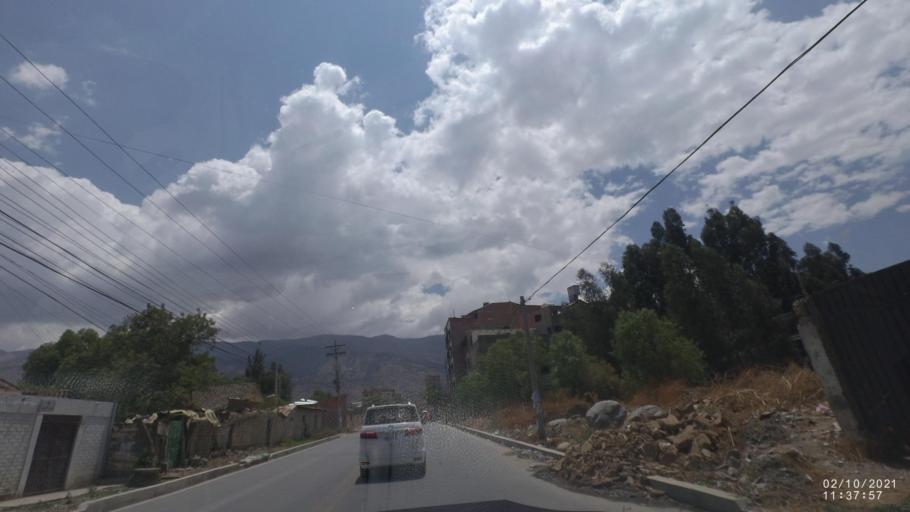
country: BO
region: Cochabamba
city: Cochabamba
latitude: -17.3417
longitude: -66.2224
